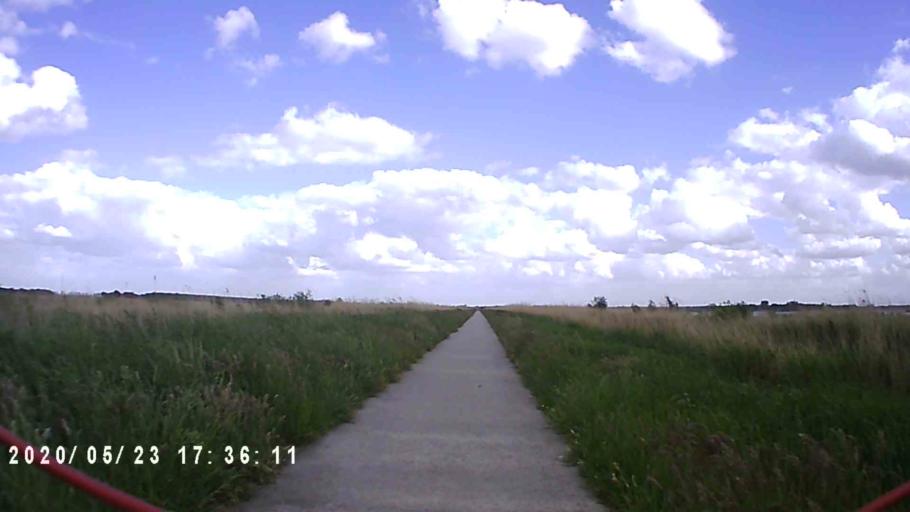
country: NL
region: Groningen
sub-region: Gemeente Slochteren
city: Slochteren
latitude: 53.2478
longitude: 6.7745
